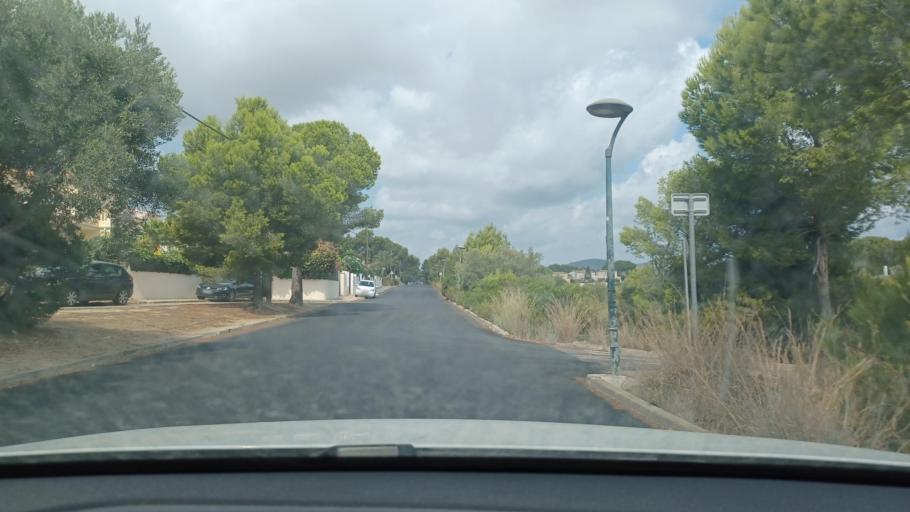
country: ES
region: Catalonia
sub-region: Provincia de Tarragona
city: l'Ametlla de Mar
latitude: 40.9061
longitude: 0.8152
